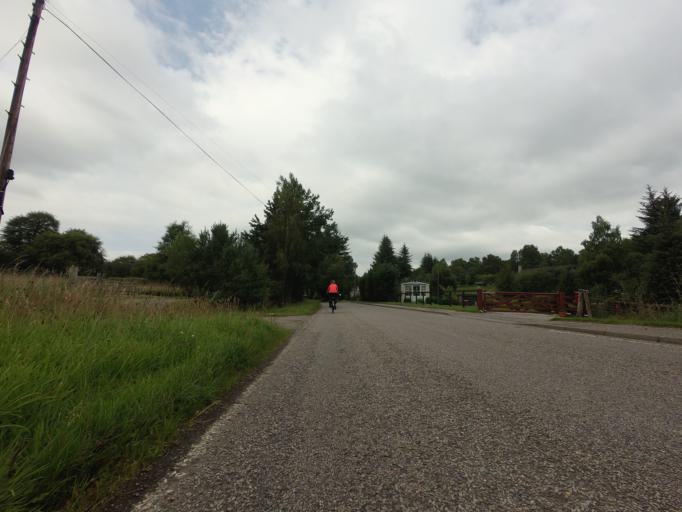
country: GB
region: Scotland
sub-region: Highland
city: Evanton
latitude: 57.9426
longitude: -4.4072
